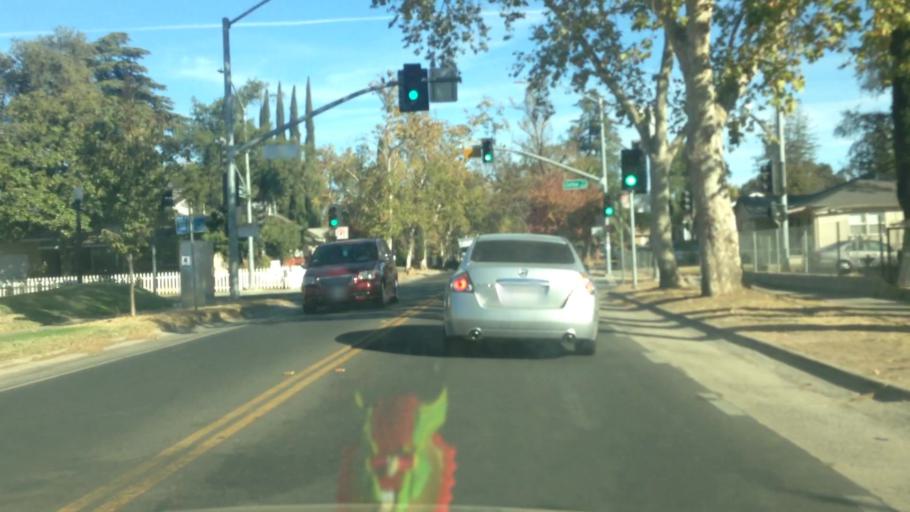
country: US
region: California
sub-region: Sacramento County
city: Sacramento
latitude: 38.6111
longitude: -121.4648
